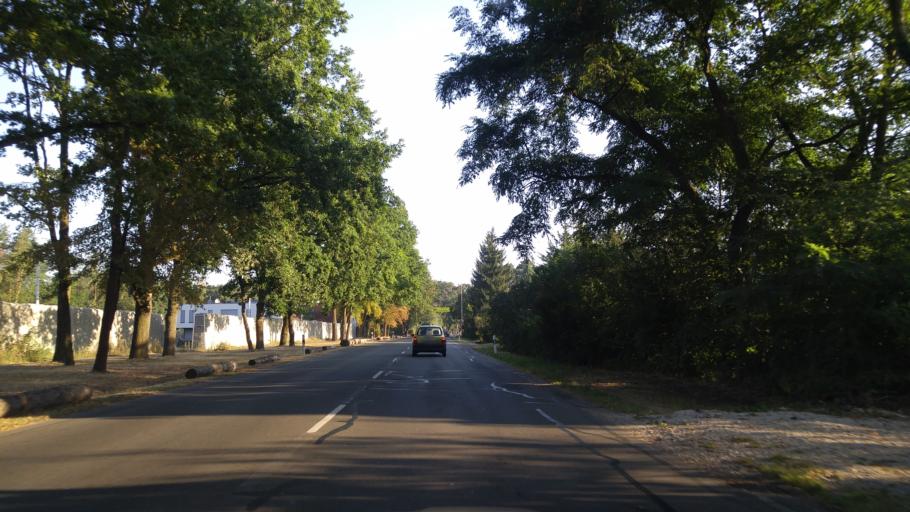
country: DE
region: Bavaria
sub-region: Regierungsbezirk Mittelfranken
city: Erlangen
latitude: 49.5458
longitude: 10.9855
